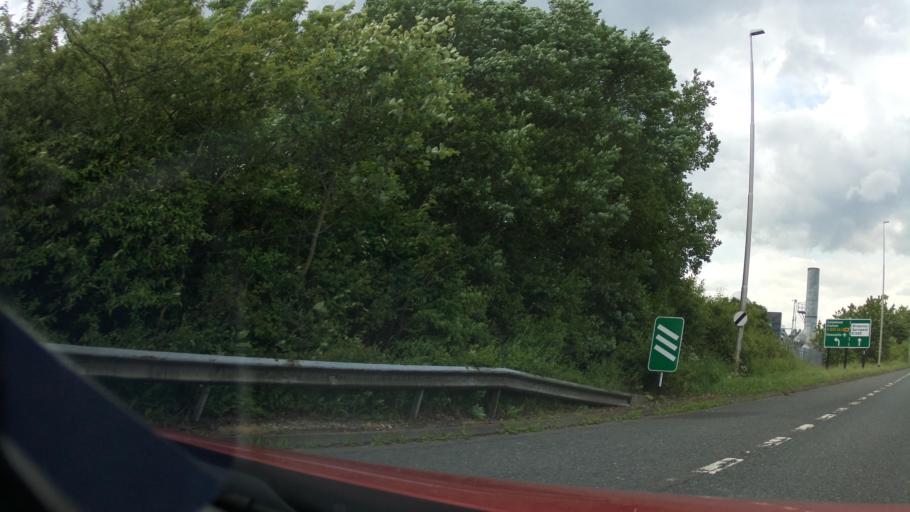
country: GB
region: England
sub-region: Sunderland
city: Washington
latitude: 54.9035
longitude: -1.5539
